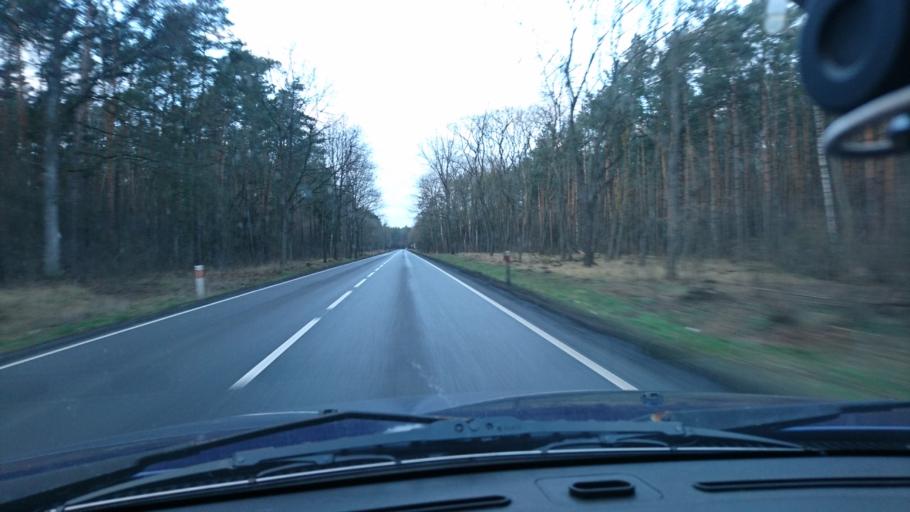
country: PL
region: Greater Poland Voivodeship
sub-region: Powiat kepinski
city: Kepno
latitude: 51.3334
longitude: 17.9570
